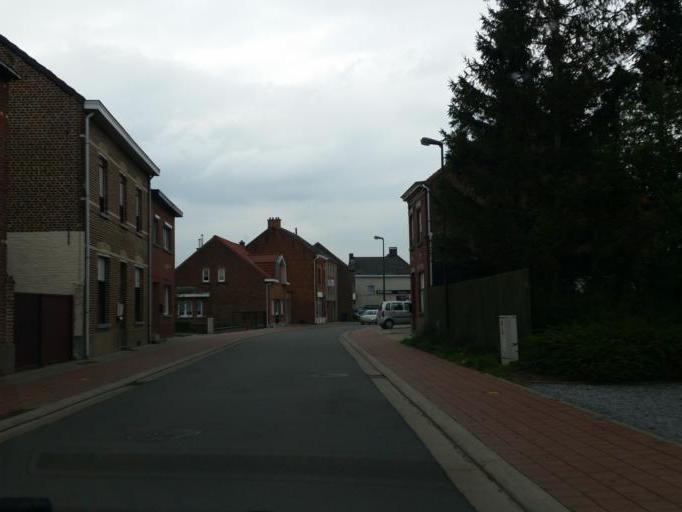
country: BE
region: Flanders
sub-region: Provincie Vlaams-Brabant
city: Kampenhout
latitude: 50.9174
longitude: 4.5635
